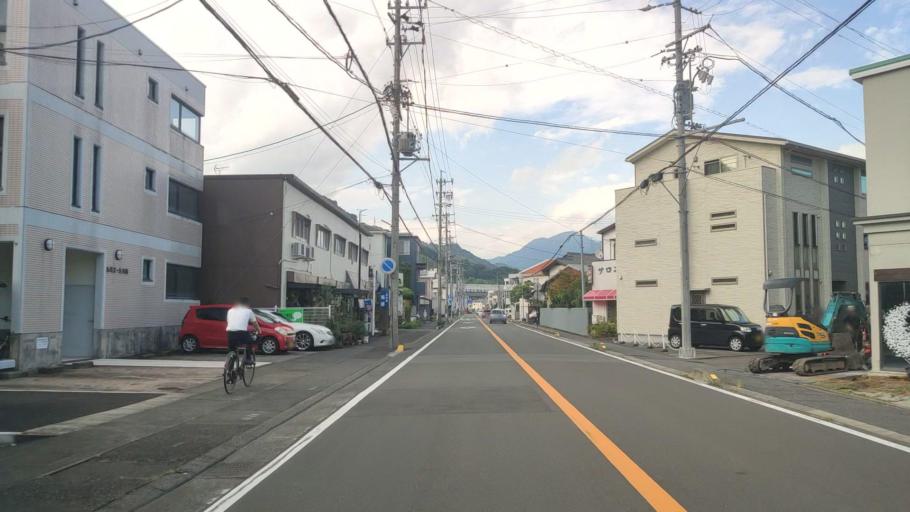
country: JP
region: Shizuoka
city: Shizuoka-shi
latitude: 35.0006
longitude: 138.3831
